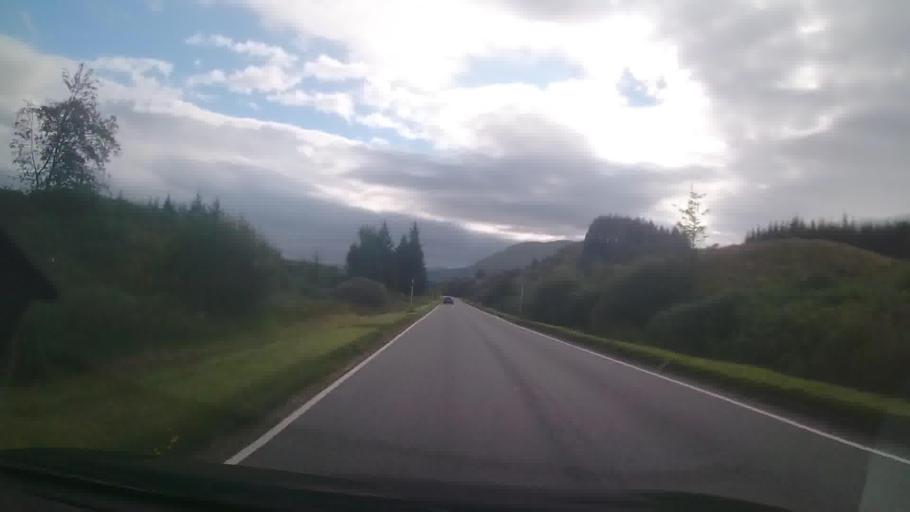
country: GB
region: Scotland
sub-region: Argyll and Bute
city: Garelochhead
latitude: 56.3283
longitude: -5.0756
